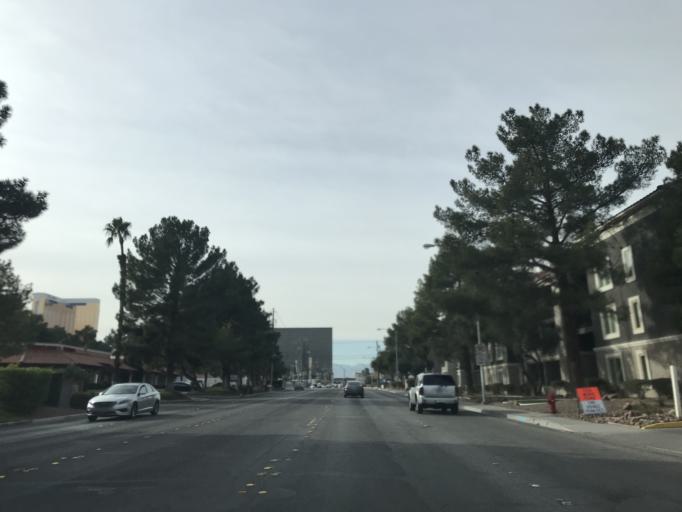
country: US
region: Nevada
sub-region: Clark County
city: Paradise
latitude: 36.0973
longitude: -115.1667
